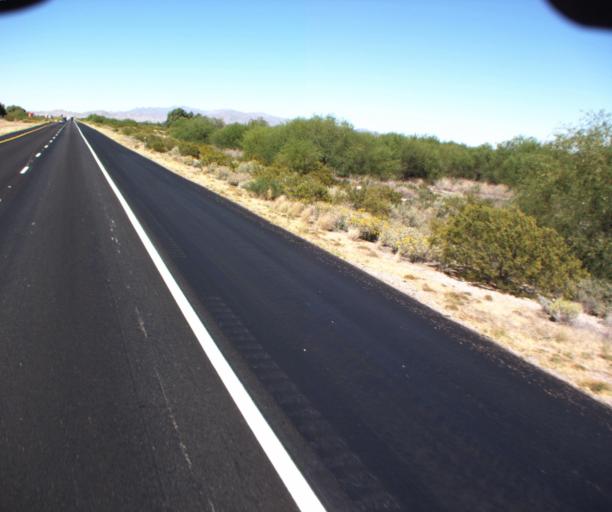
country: US
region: Arizona
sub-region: Maricopa County
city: Buckeye
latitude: 33.3209
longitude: -112.6229
